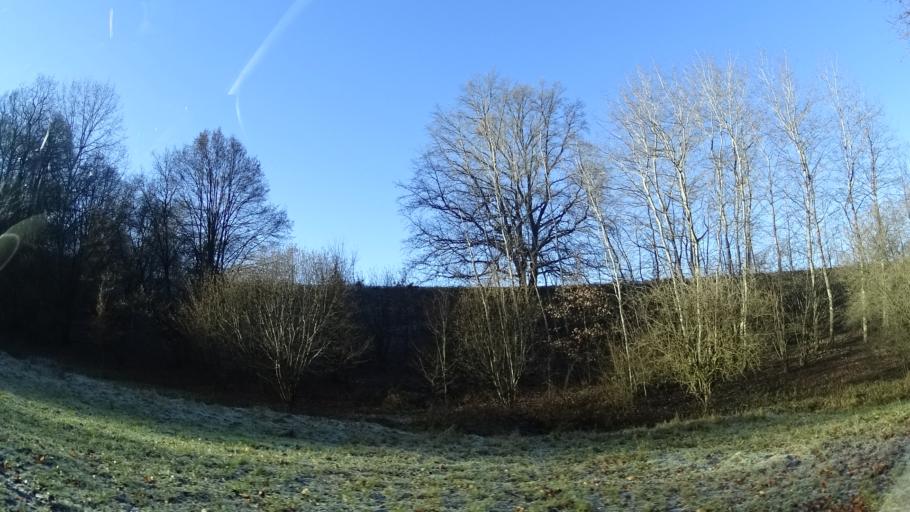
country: DE
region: Thuringia
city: Lindig
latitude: 50.7923
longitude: 11.5927
